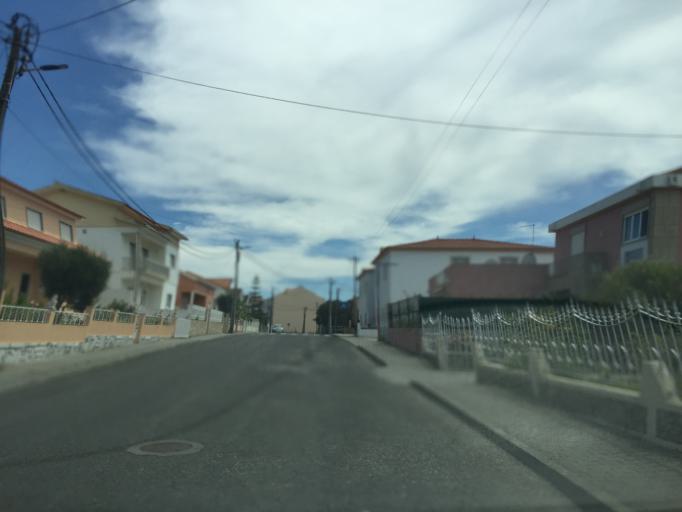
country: PT
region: Lisbon
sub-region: Lourinha
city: Lourinha
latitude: 39.2030
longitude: -9.3343
